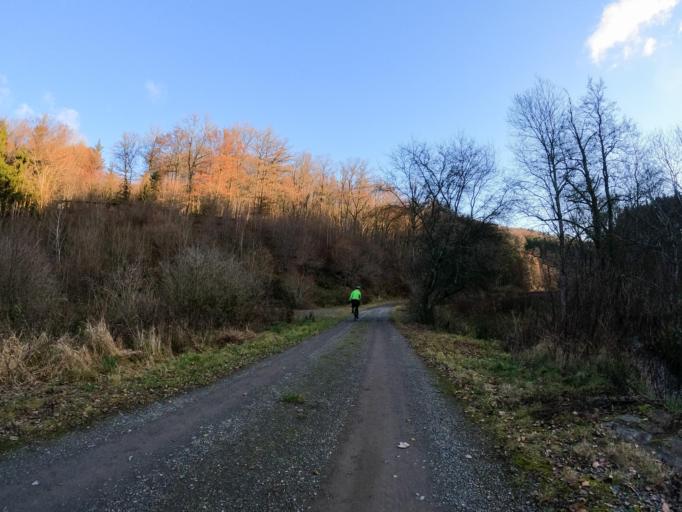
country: LU
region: Diekirch
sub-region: Canton de Wiltz
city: Bavigne
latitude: 49.9509
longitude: 5.8389
